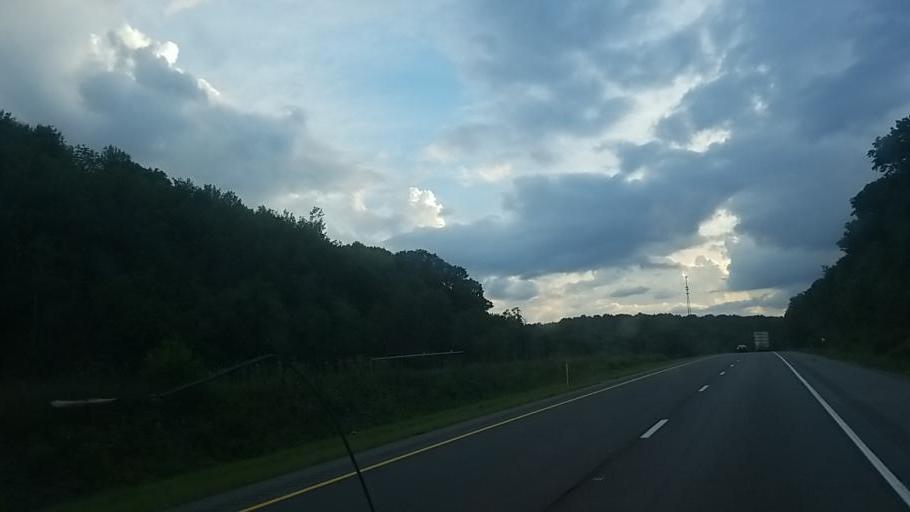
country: US
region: Pennsylvania
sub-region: Clearfield County
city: Treasure Lake
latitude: 41.1210
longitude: -78.6246
